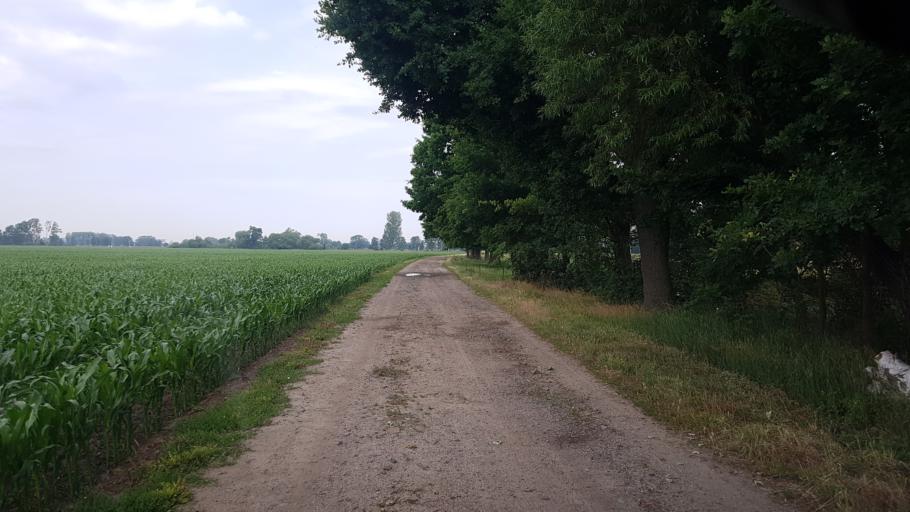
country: DE
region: Brandenburg
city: Schonewalde
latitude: 51.6797
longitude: 13.5978
